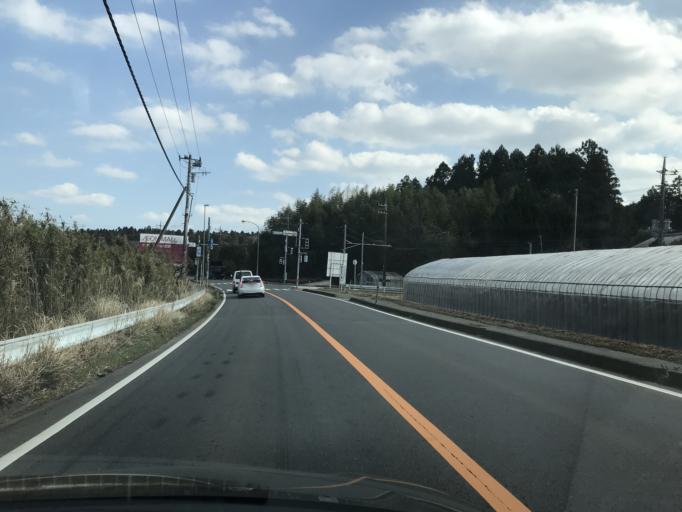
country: JP
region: Chiba
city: Sawara
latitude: 35.8162
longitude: 140.5132
